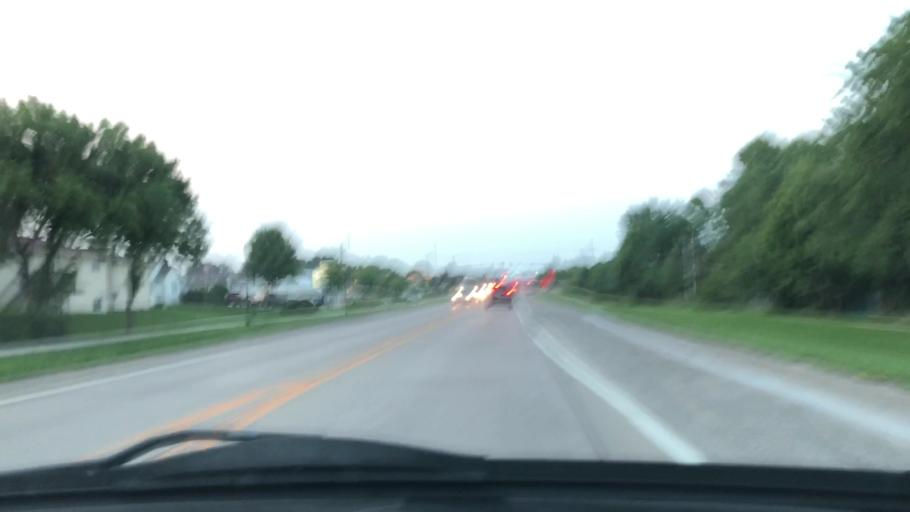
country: US
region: Iowa
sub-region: Johnson County
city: North Liberty
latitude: 41.7423
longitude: -91.6076
